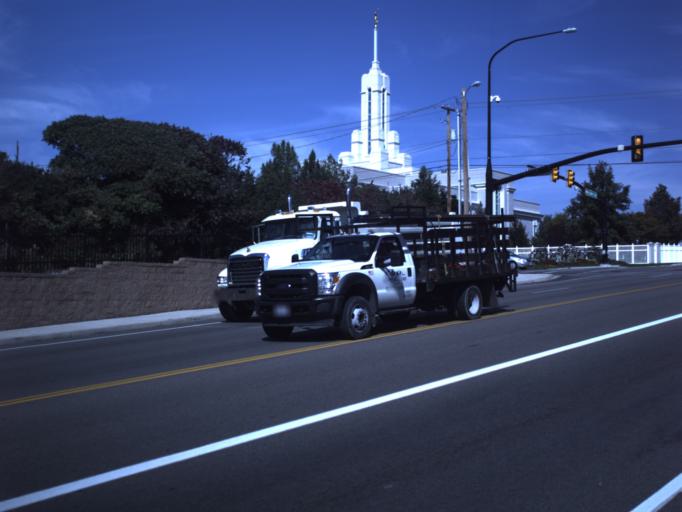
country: US
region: Utah
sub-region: Utah County
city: Cedar Hills
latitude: 40.3914
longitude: -111.7690
